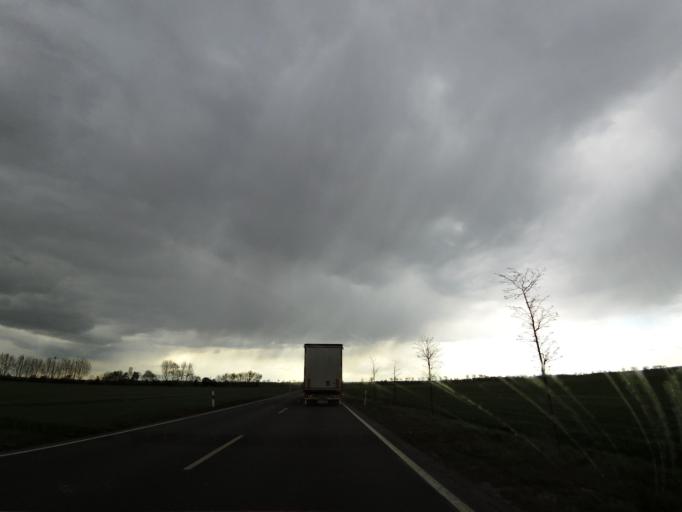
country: DE
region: Saxony-Anhalt
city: Kroppenstedt
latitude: 51.9401
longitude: 11.3359
